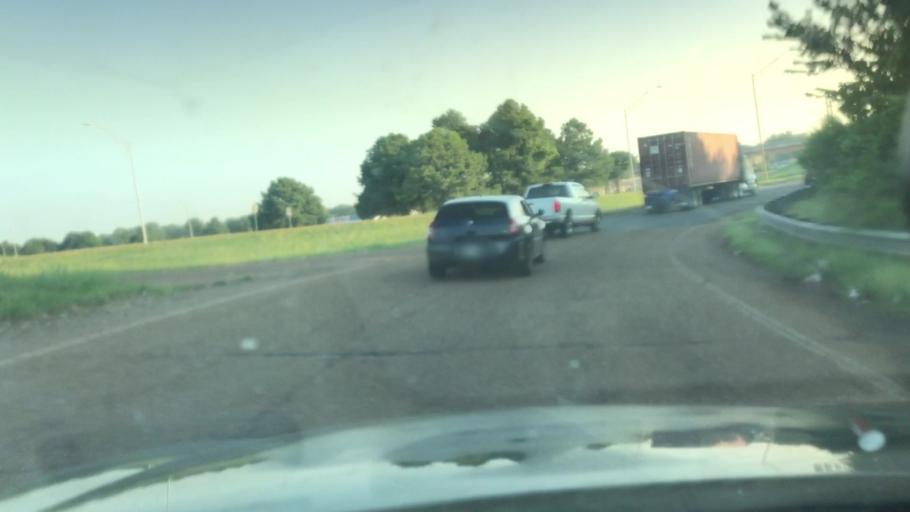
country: US
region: Tennessee
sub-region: Shelby County
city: New South Memphis
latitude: 35.0786
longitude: -89.9535
